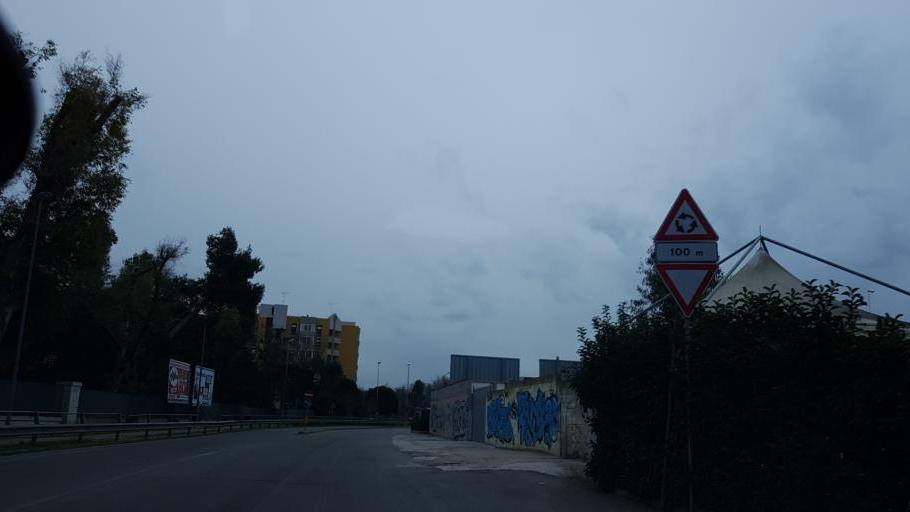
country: IT
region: Apulia
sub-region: Provincia di Brindisi
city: Brindisi
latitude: 40.6277
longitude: 17.9198
